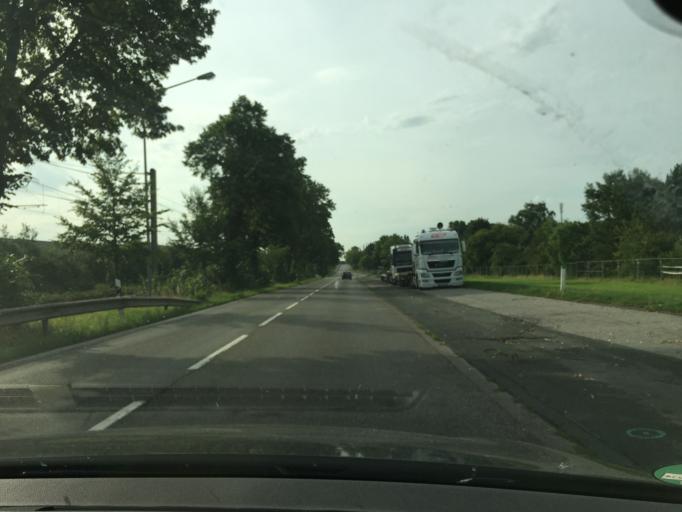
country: DE
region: North Rhine-Westphalia
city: Wesseling
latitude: 50.8134
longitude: 6.9982
